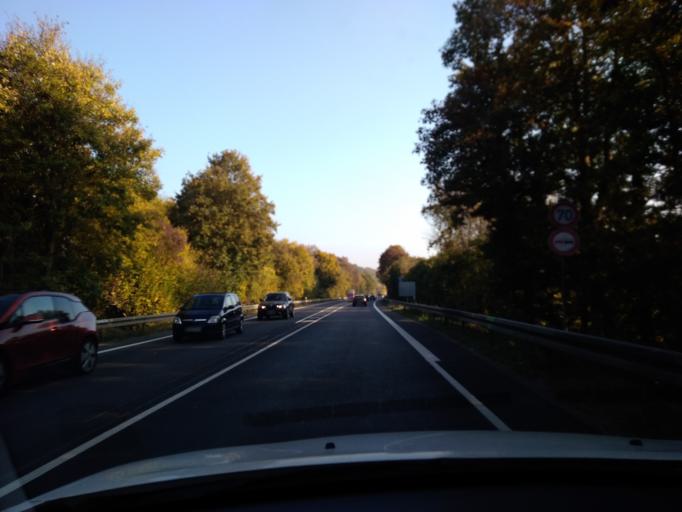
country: FR
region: Lorraine
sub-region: Departement de la Moselle
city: Alsting
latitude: 49.2014
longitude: 7.0236
